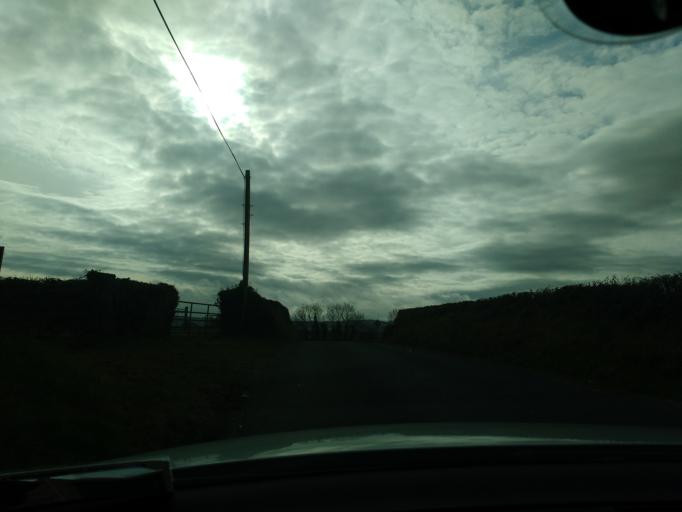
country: IE
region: Leinster
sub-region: Laois
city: Rathdowney
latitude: 52.6828
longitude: -7.6121
